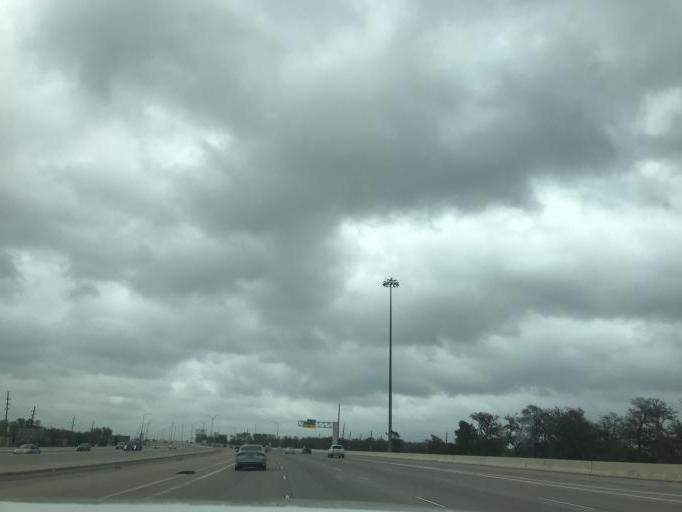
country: US
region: Texas
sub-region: Fort Bend County
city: Greatwood
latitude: 29.5646
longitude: -95.6745
